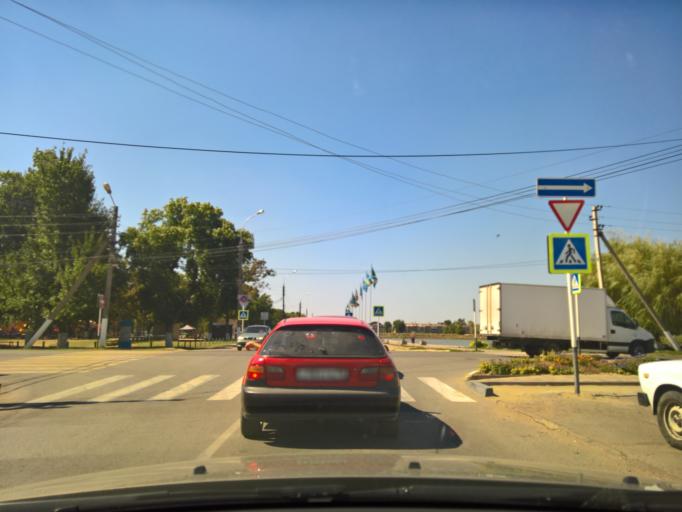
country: RU
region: Krasnodarskiy
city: Slavyansk-na-Kubani
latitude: 45.2630
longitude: 38.1069
